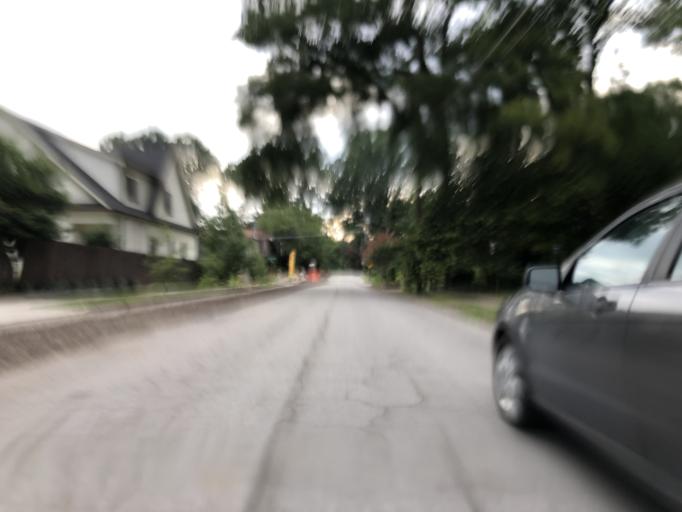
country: US
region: Georgia
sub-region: DeKalb County
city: Decatur
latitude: 33.7784
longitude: -84.3016
